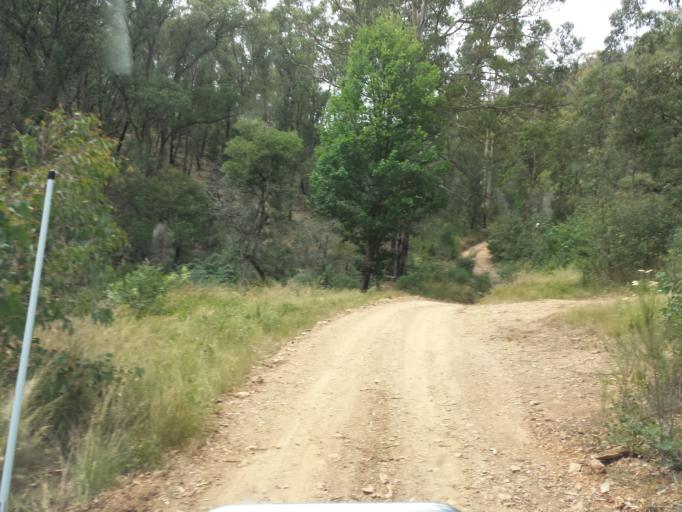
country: AU
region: Victoria
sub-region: Wellington
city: Heyfield
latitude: -37.7543
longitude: 146.5016
